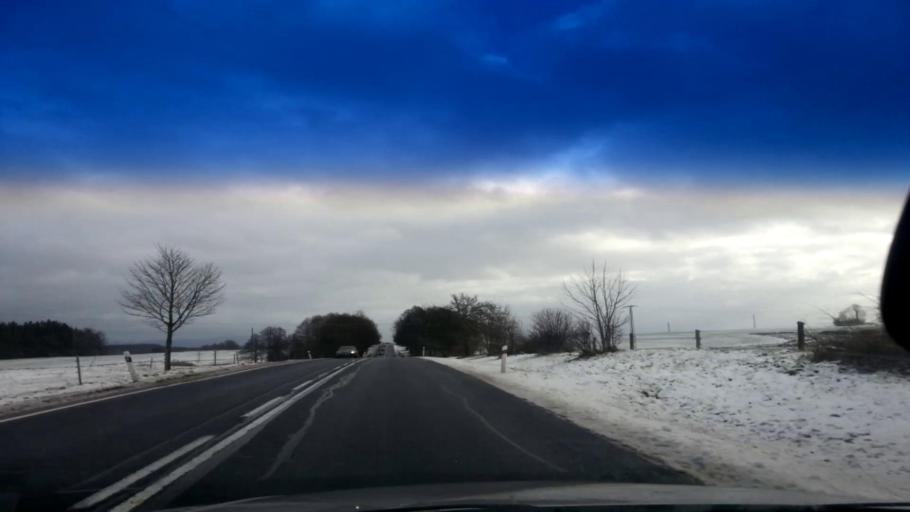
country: CZ
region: Karlovarsky
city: Hazlov
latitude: 50.1517
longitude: 12.2860
